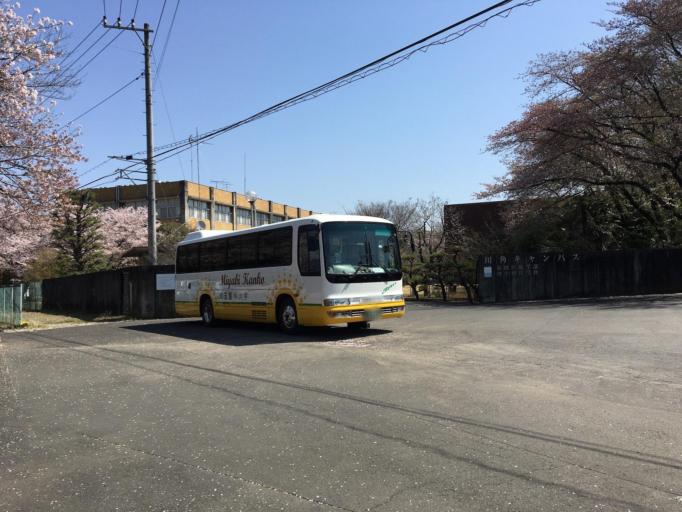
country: JP
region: Saitama
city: Morohongo
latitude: 35.9550
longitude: 139.3421
